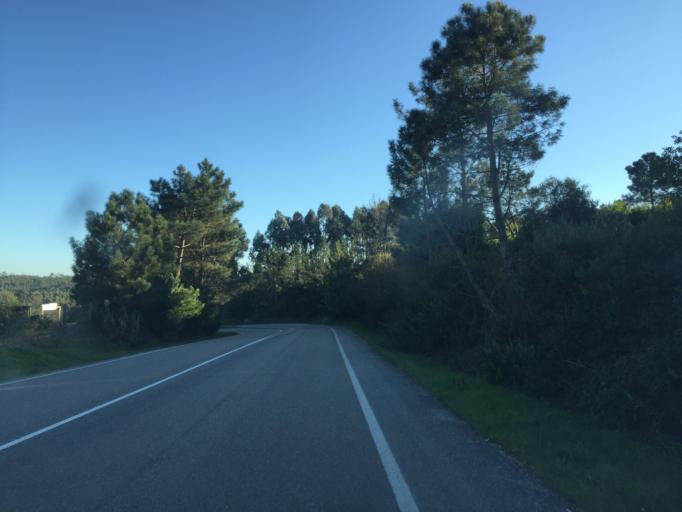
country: PT
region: Coimbra
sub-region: Figueira da Foz
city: Alhadas
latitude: 40.1560
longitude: -8.7985
